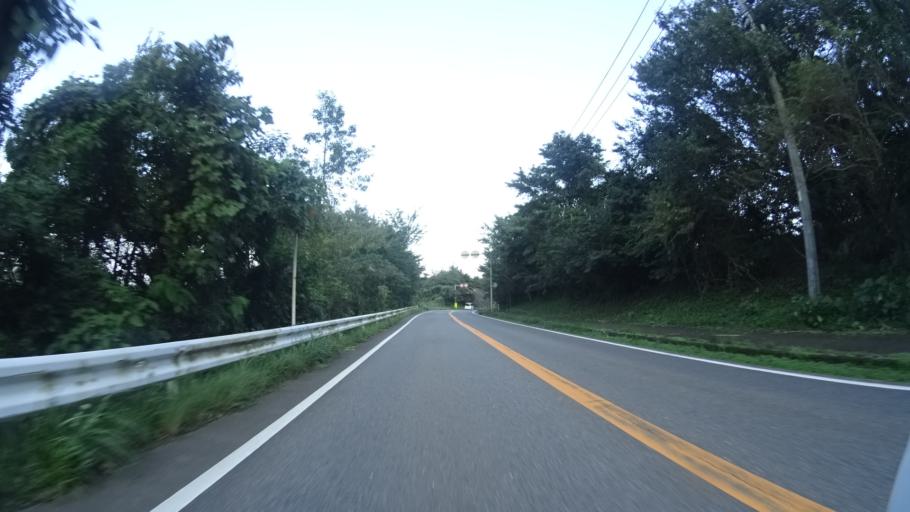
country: JP
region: Oita
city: Hiji
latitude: 33.3513
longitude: 131.4496
